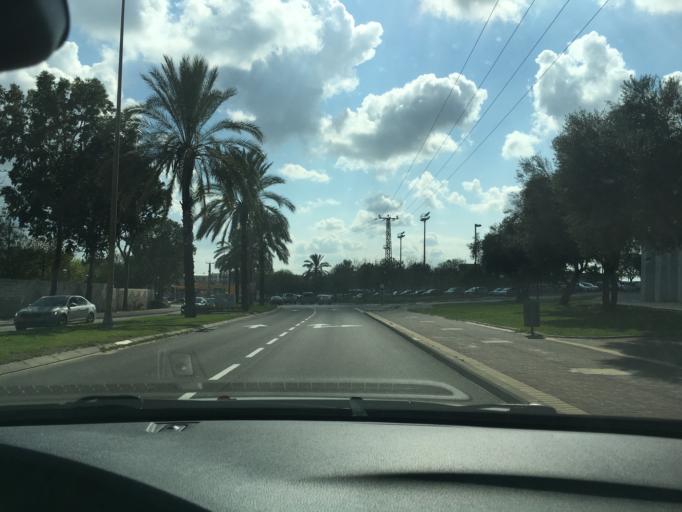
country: IL
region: Central District
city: Kfar Saba
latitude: 32.1810
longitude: 34.9279
